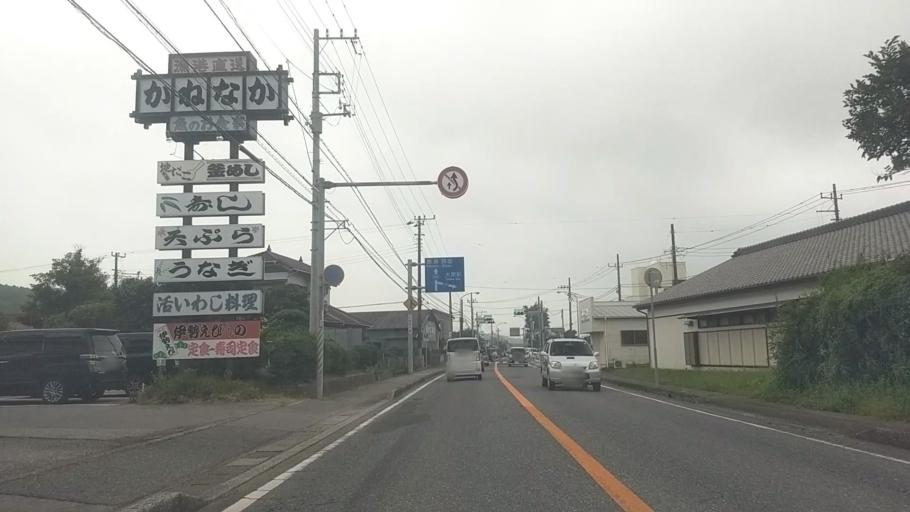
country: JP
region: Chiba
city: Ohara
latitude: 35.2377
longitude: 140.3905
